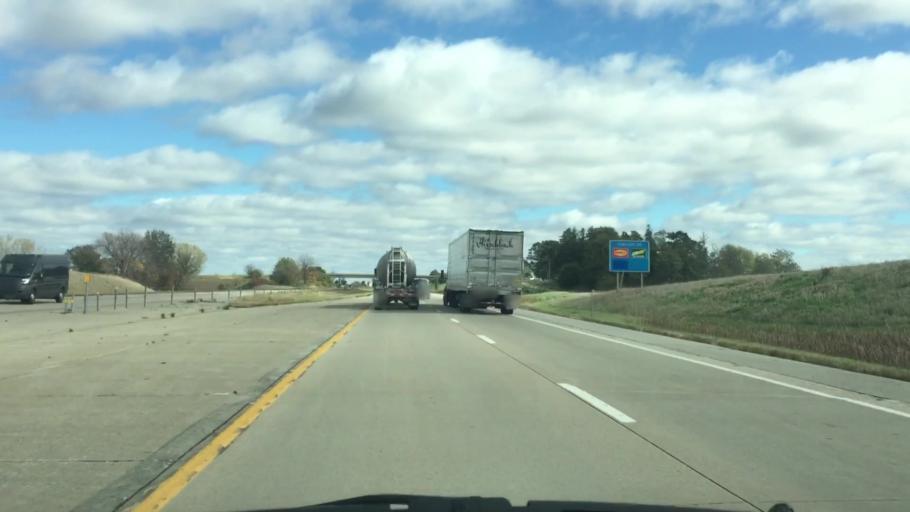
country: US
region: Iowa
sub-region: Poweshiek County
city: Brooklyn
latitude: 41.6961
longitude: -92.4022
